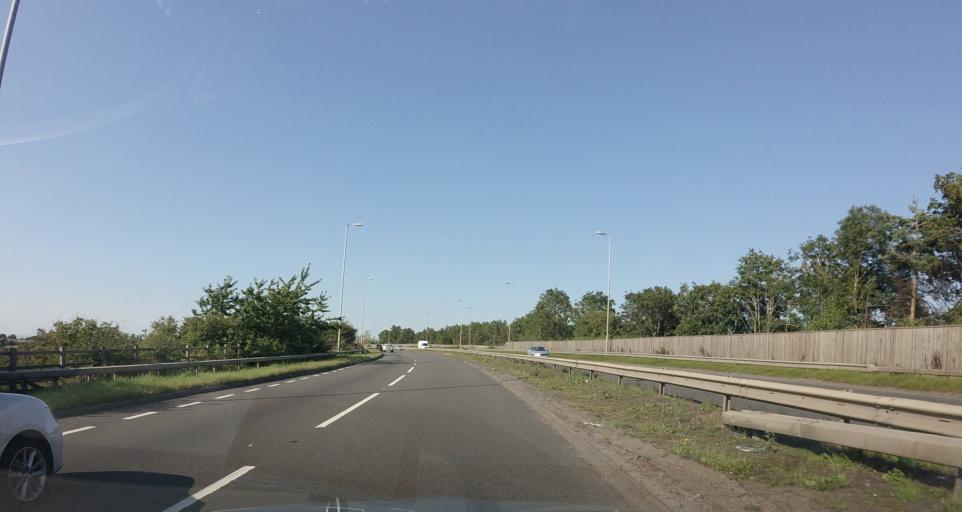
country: GB
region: Scotland
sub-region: North Lanarkshire
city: Bellshill
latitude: 55.8117
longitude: -4.0381
